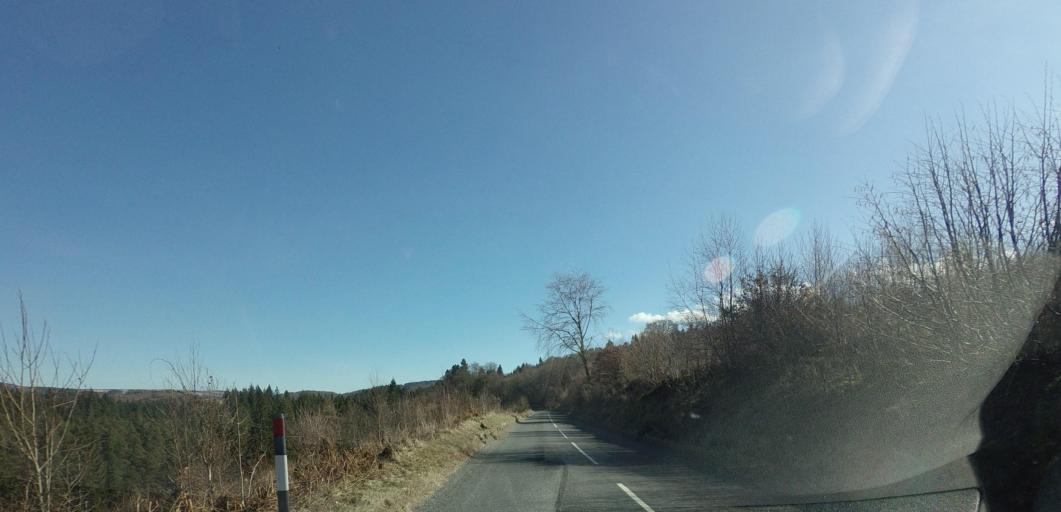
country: GB
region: Scotland
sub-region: Perth and Kinross
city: Bankfoot
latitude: 56.5546
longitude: -3.6221
